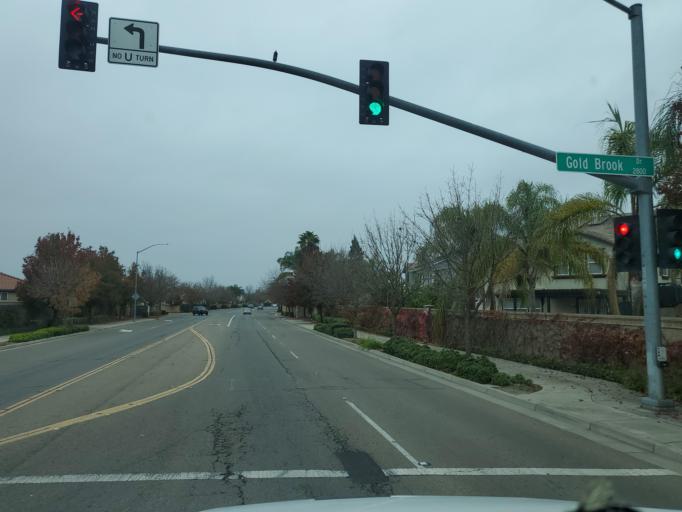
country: US
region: California
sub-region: San Joaquin County
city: August
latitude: 38.0017
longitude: -121.2709
